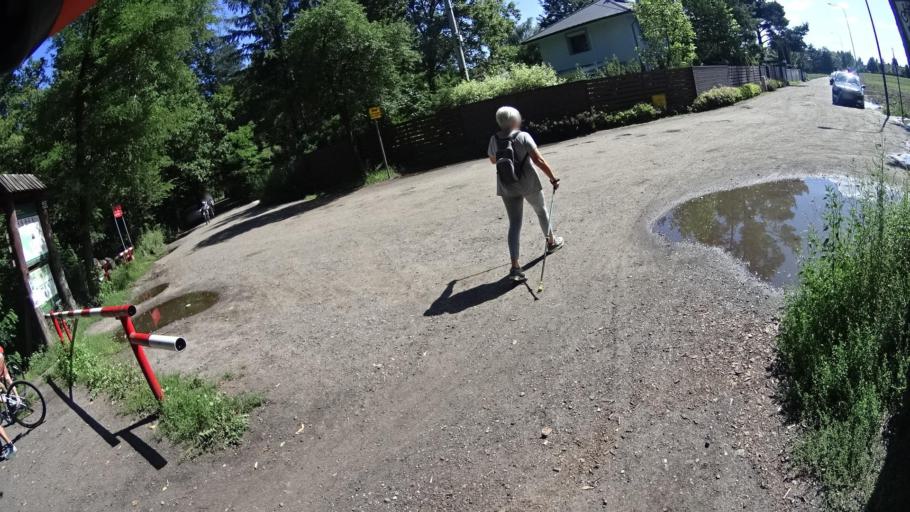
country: PL
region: Masovian Voivodeship
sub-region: Powiat piaseczynski
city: Jozefoslaw
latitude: 52.1089
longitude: 21.0560
